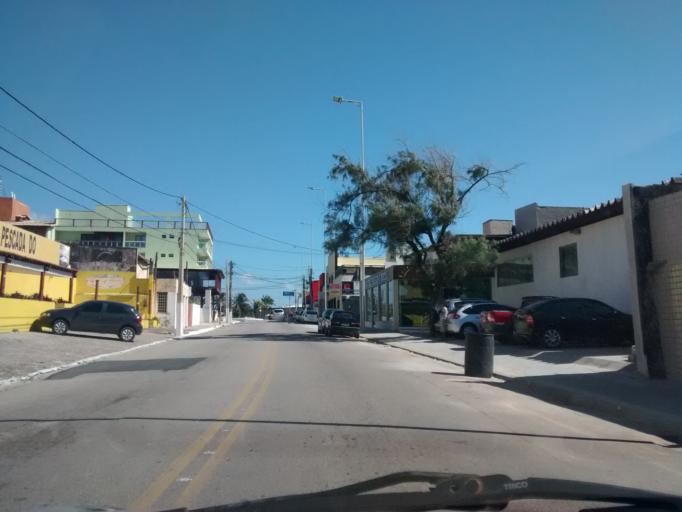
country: BR
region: Rio Grande do Norte
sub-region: Natal
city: Natal
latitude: -5.7848
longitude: -35.1904
